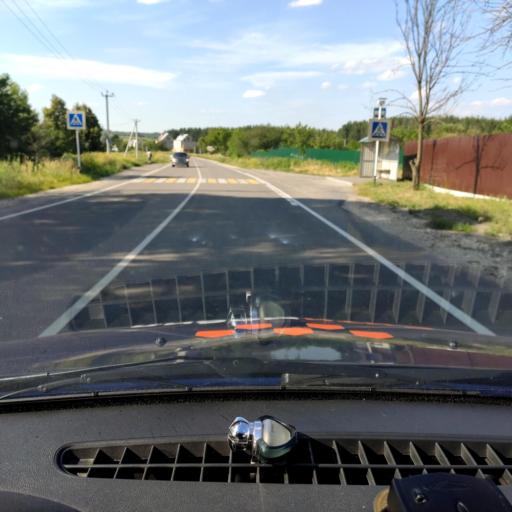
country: RU
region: Voronezj
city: Devitsa
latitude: 51.6501
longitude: 38.9727
